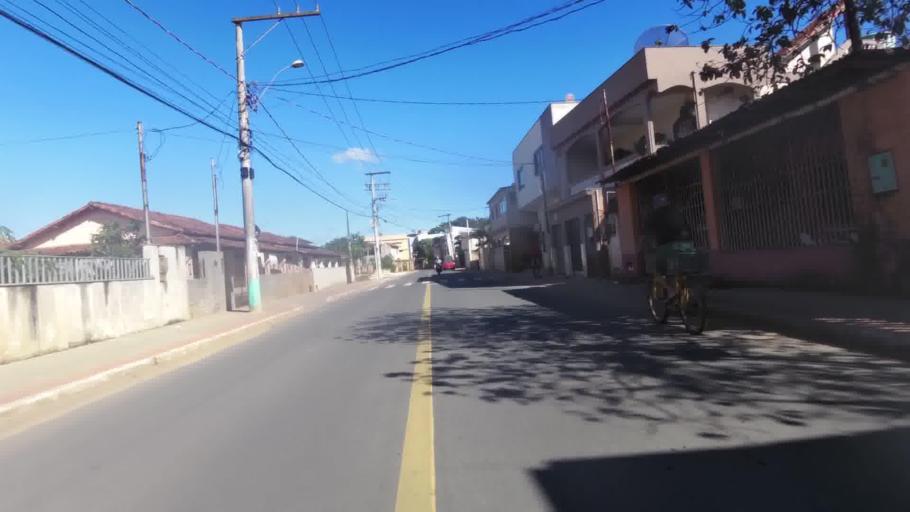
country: BR
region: Espirito Santo
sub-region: Piuma
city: Piuma
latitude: -20.8399
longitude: -40.7345
